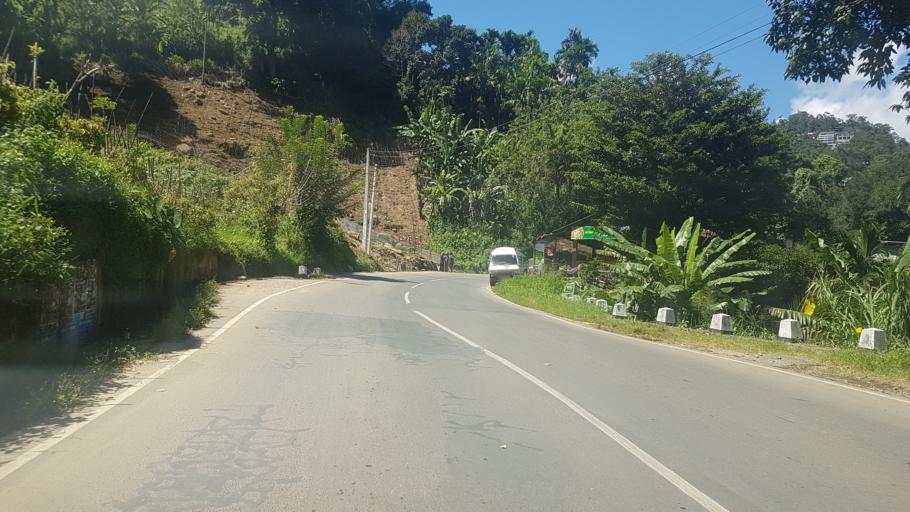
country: LK
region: Uva
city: Badulla
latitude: 6.8662
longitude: 81.0514
